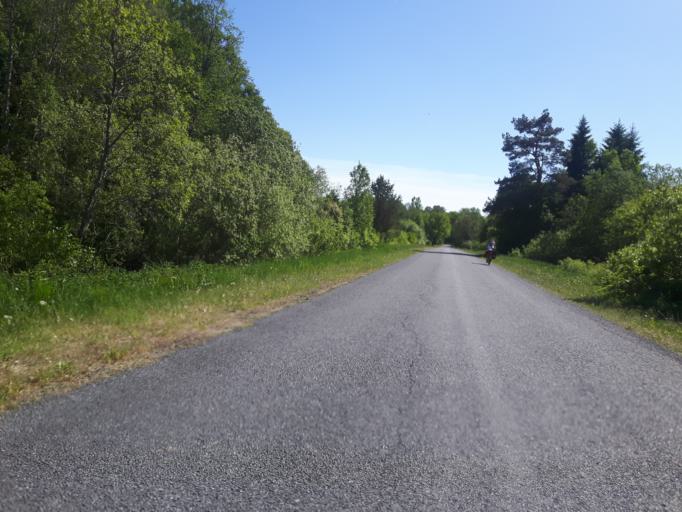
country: EE
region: Laeaene-Virumaa
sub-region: Haljala vald
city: Haljala
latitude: 59.5442
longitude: 26.2367
